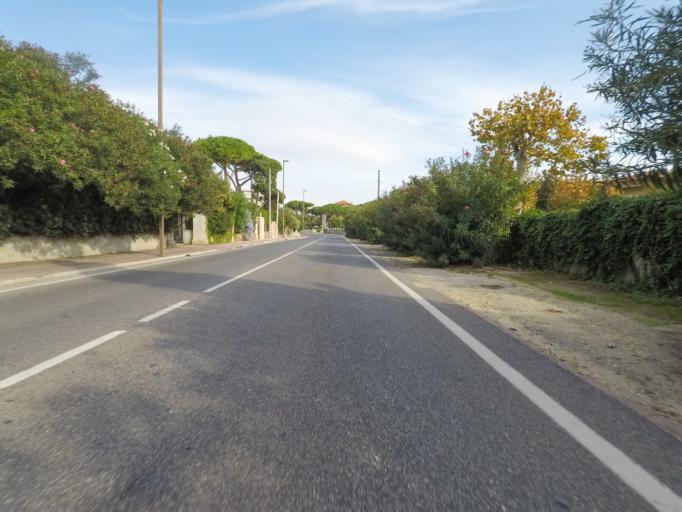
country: IT
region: Latium
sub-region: Citta metropolitana di Roma Capitale
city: Santa Marinella
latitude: 42.0322
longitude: 11.8437
